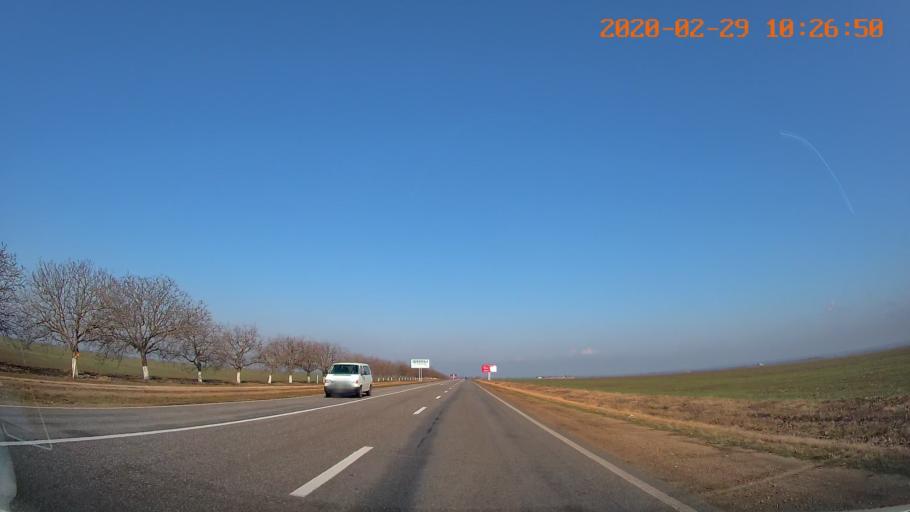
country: MD
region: Telenesti
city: Tiraspolul Nou
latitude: 46.8885
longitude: 29.6011
